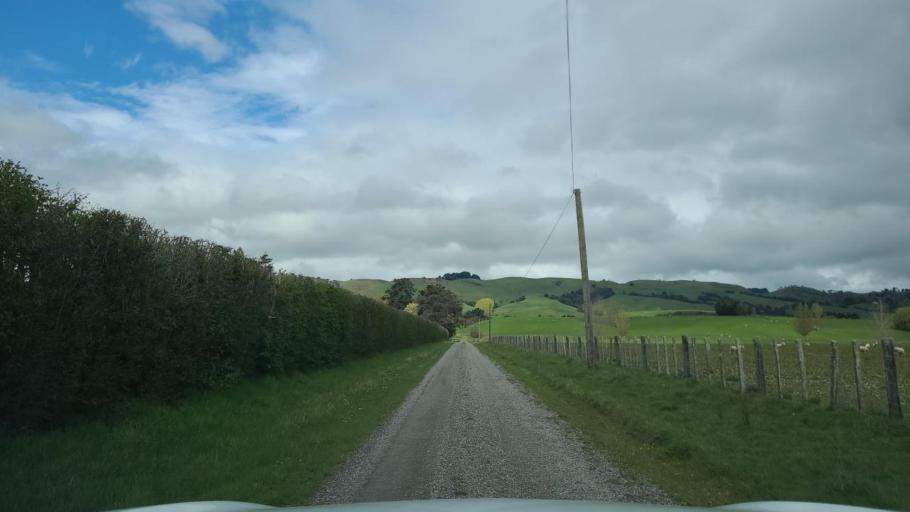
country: NZ
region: Wellington
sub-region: Masterton District
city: Masterton
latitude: -41.0811
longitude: 175.6609
